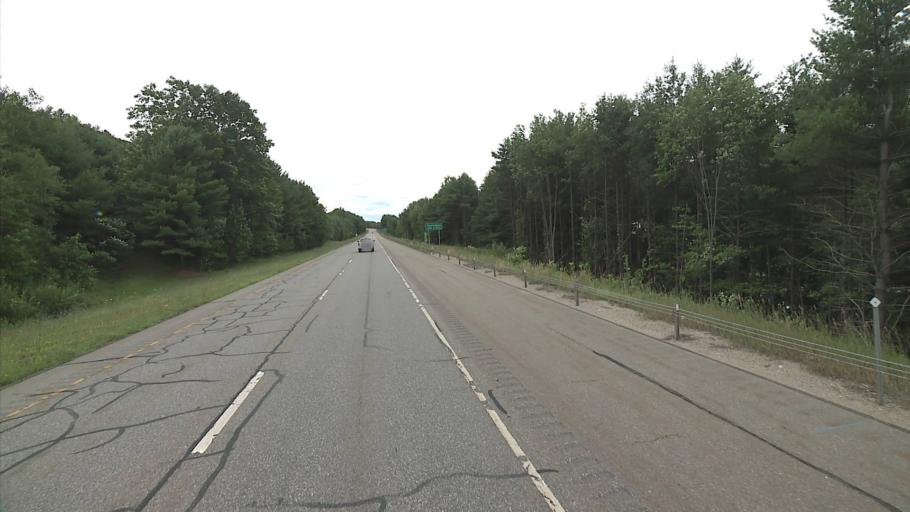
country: US
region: Connecticut
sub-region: Litchfield County
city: Winsted
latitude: 41.9003
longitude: -73.0670
